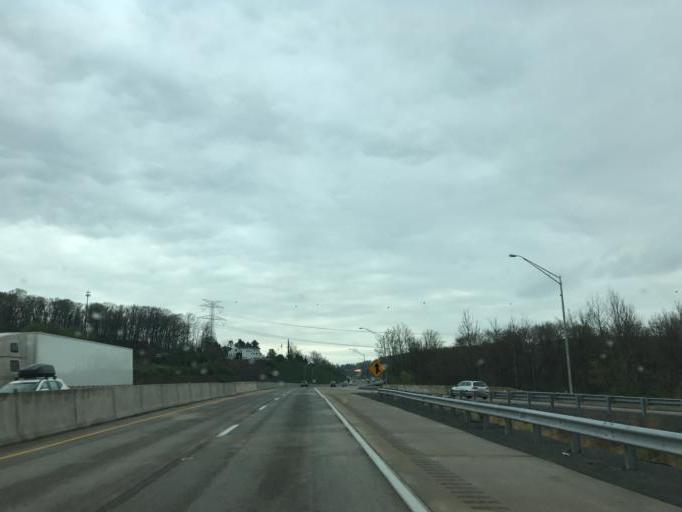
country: US
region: Pennsylvania
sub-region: Lancaster County
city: Adamstown
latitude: 40.2484
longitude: -76.0369
